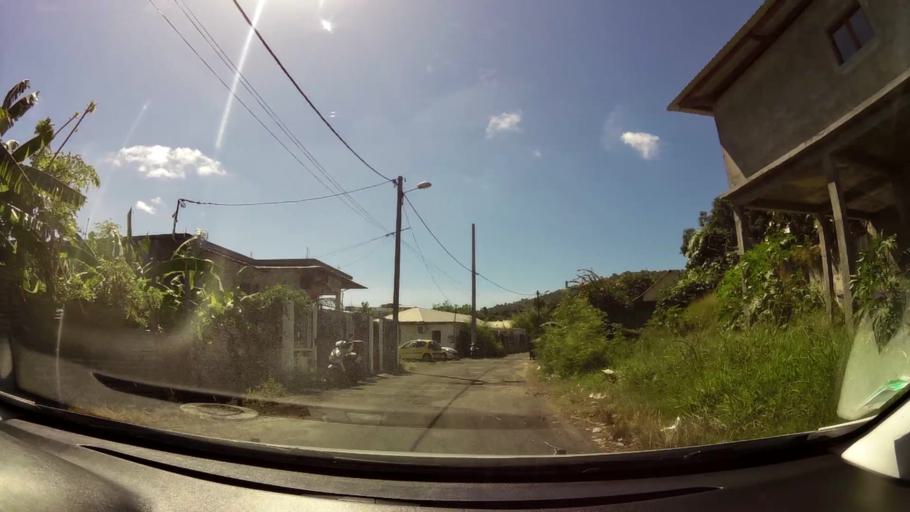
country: YT
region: Pamandzi
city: Pamandzi
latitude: -12.8003
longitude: 45.2790
